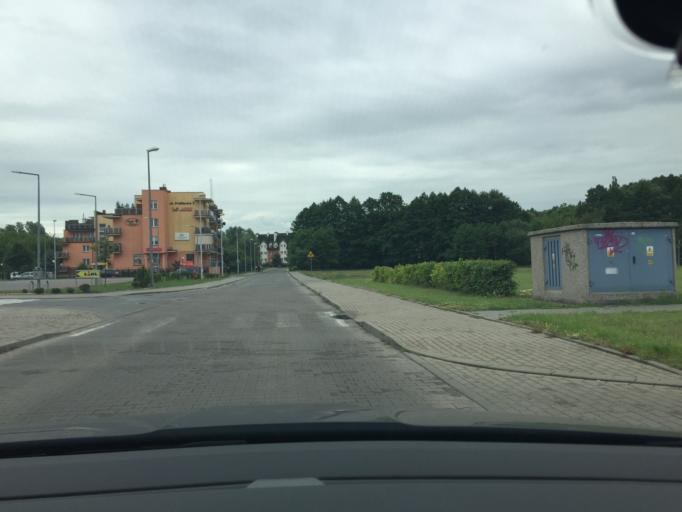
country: PL
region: Kujawsko-Pomorskie
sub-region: Torun
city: Torun
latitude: 52.9946
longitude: 18.5997
